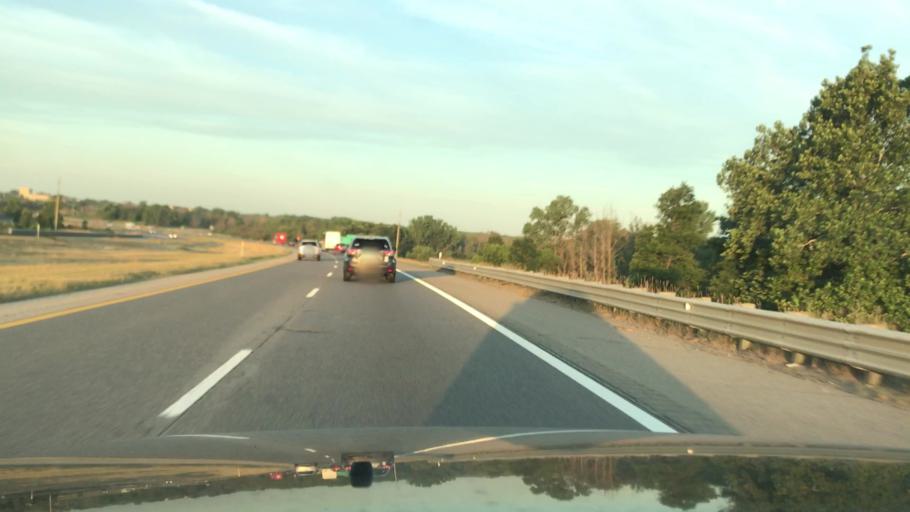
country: US
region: Michigan
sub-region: Ottawa County
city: Zeeland
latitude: 42.7915
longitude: -86.0204
